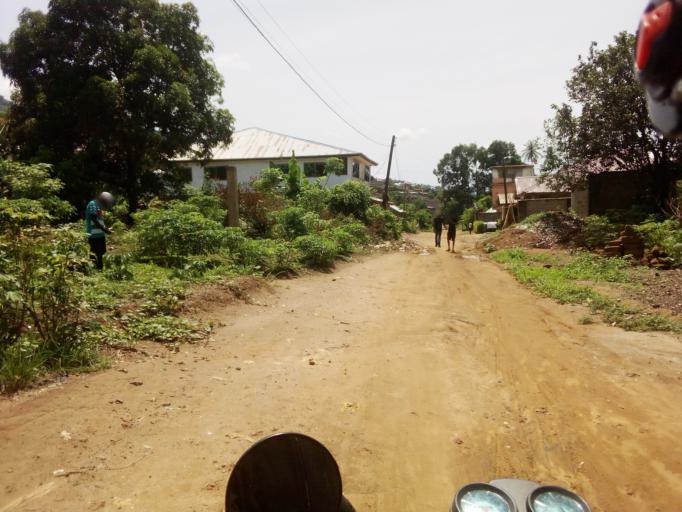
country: SL
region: Western Area
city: Waterloo
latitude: 8.3423
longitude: -13.0711
